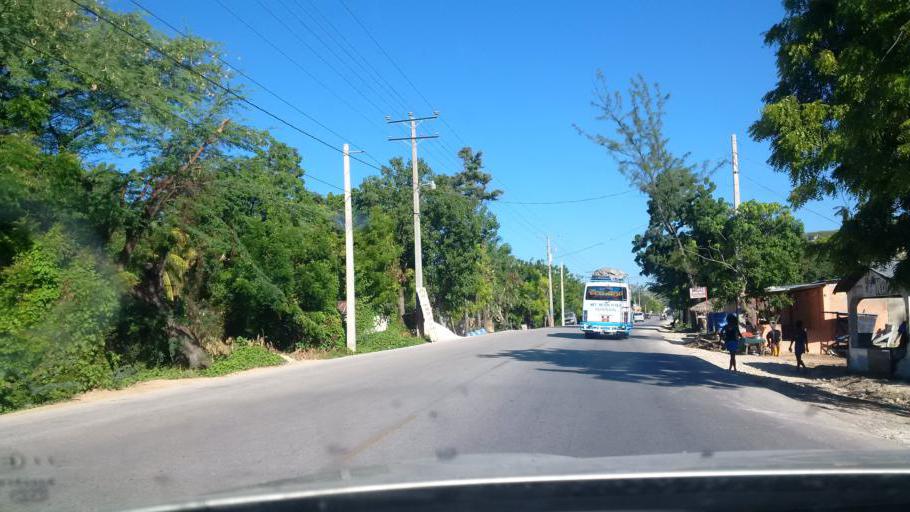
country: HT
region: Ouest
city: Cabaret
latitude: 18.7183
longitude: -72.3693
